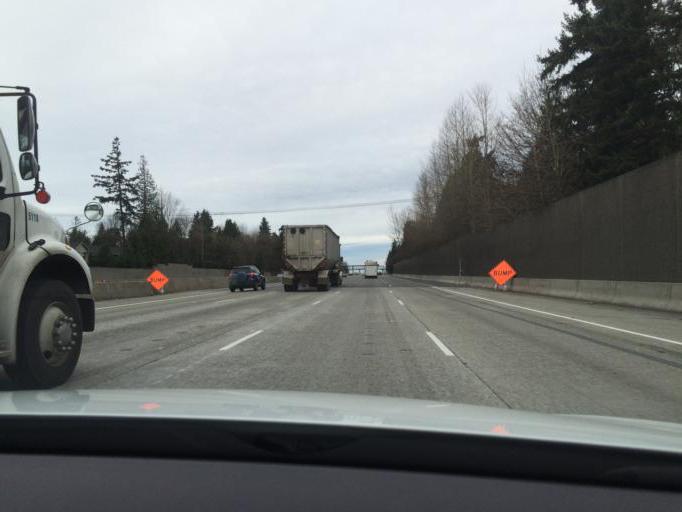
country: US
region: Washington
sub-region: King County
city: Yarrow Point
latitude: 47.6547
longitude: -122.1868
